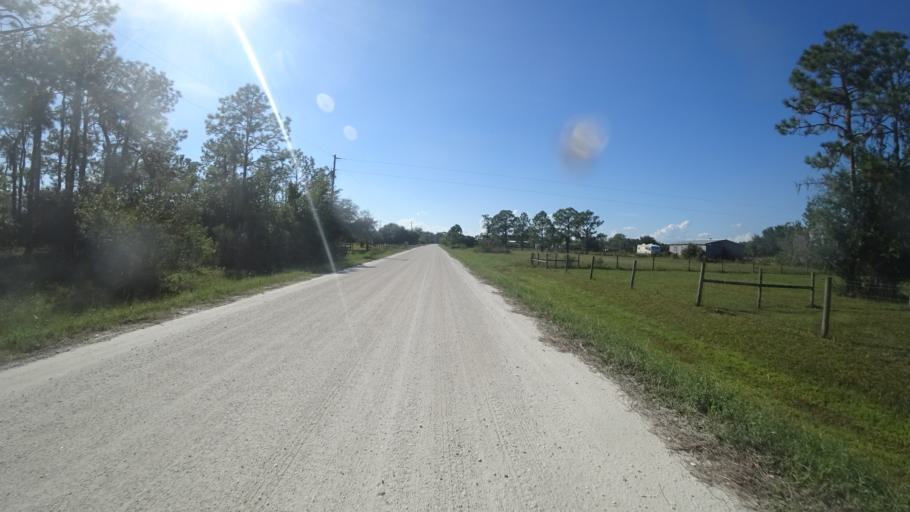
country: US
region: Florida
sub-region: Sarasota County
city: The Meadows
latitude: 27.4228
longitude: -82.2656
